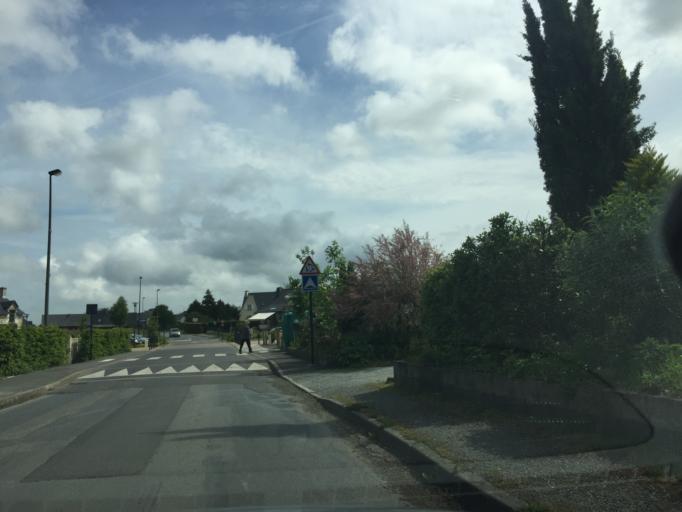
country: FR
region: Brittany
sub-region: Departement des Cotes-d'Armor
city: Corseul
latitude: 48.5120
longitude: -2.1273
